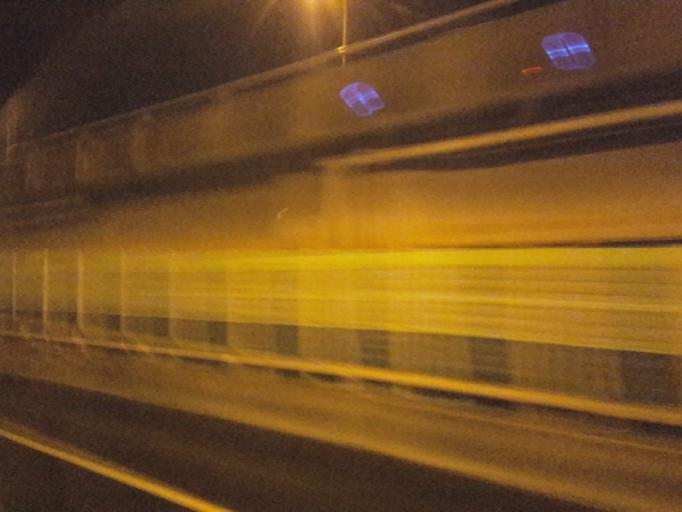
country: TW
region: Taipei
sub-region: Taipei
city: Banqiao
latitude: 25.0758
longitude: 121.4627
